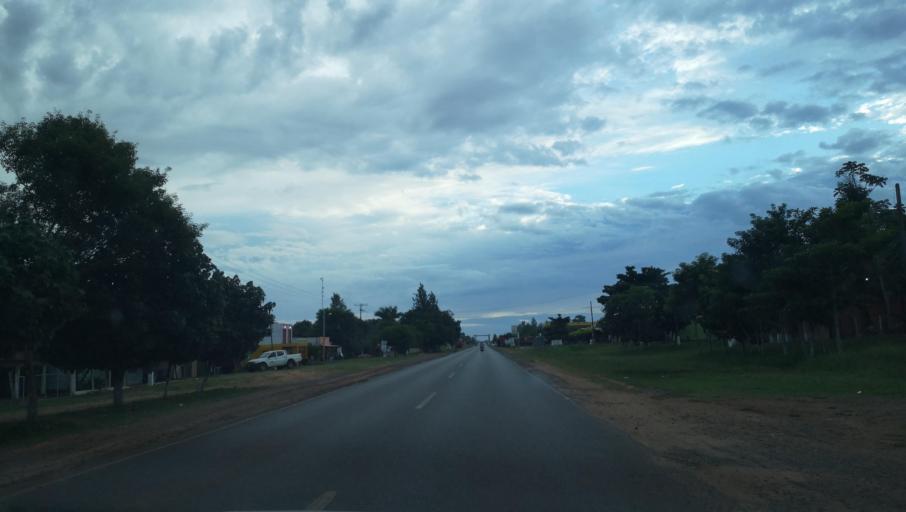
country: PY
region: San Pedro
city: Capiibary
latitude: -24.7178
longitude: -56.0142
